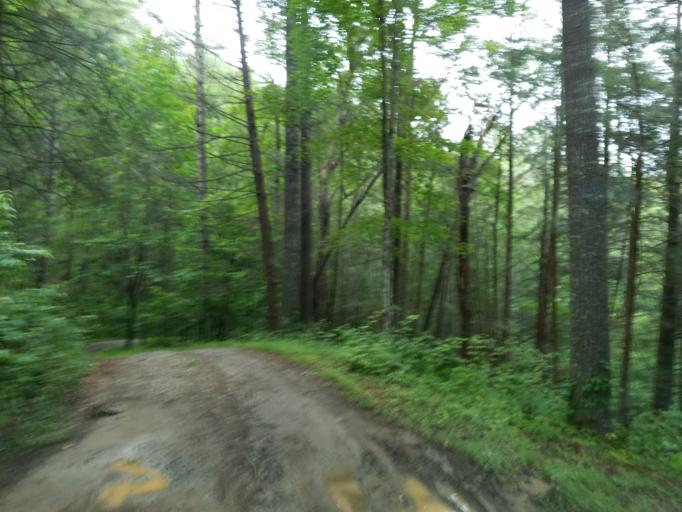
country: US
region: Georgia
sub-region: Union County
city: Blairsville
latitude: 34.7588
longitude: -84.0334
